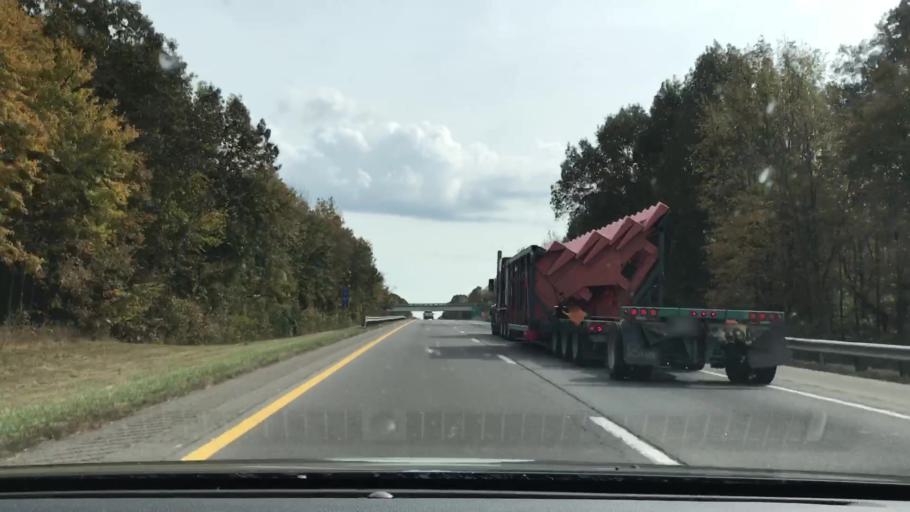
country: US
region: Tennessee
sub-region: Cheatham County
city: Pleasant View
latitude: 36.4635
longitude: -87.1202
